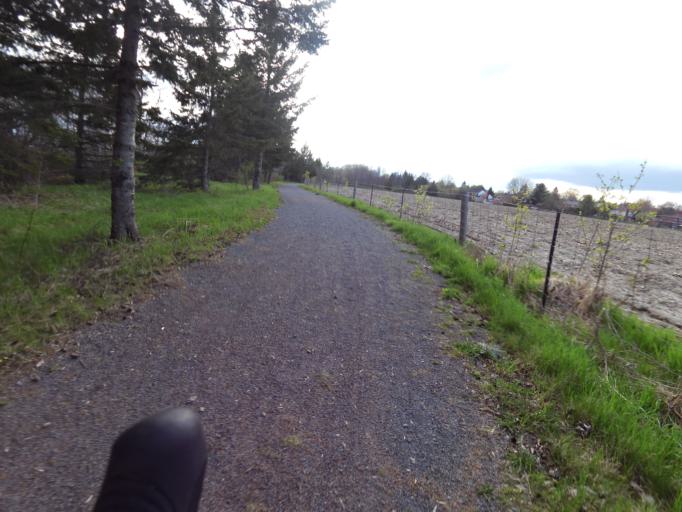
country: CA
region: Ontario
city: Ottawa
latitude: 45.3202
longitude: -75.7018
